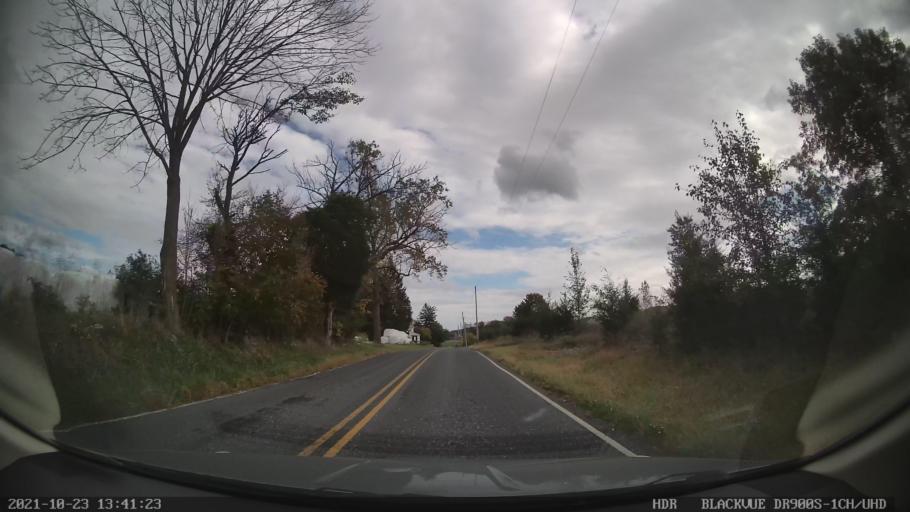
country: US
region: Pennsylvania
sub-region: Berks County
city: Bally
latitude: 40.4136
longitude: -75.5655
